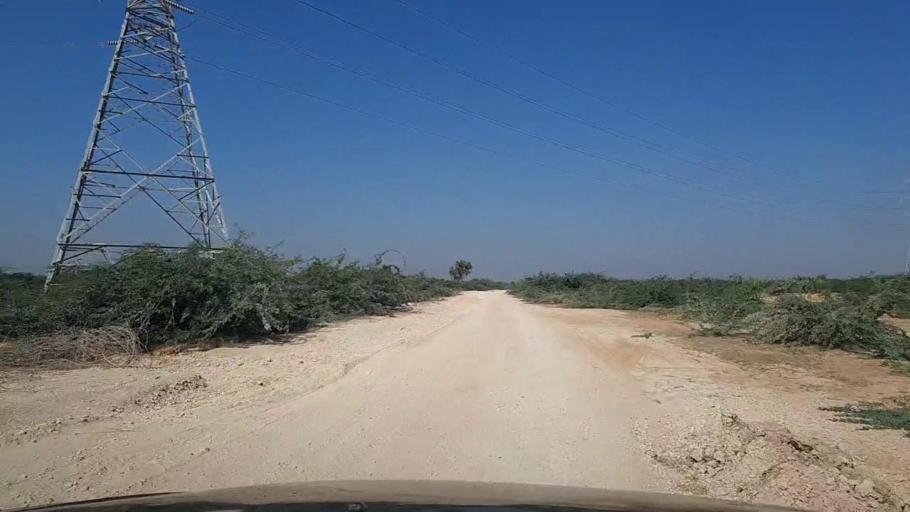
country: PK
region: Sindh
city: Thatta
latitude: 24.6242
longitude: 67.8359
